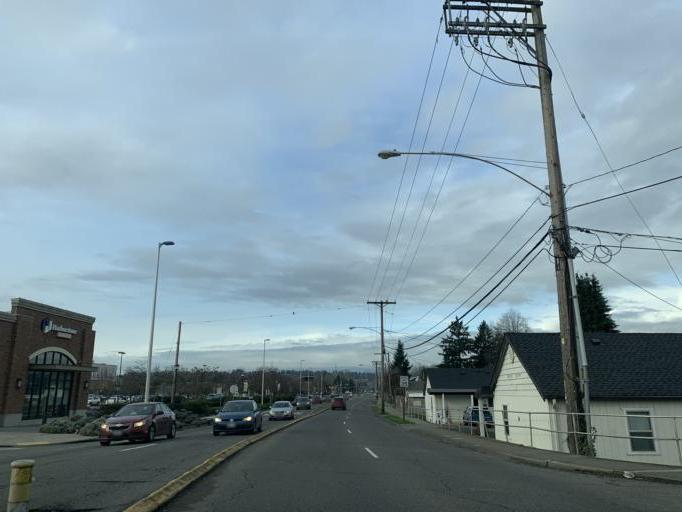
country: US
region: Washington
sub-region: King County
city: Kent
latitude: 47.3867
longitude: -122.2333
